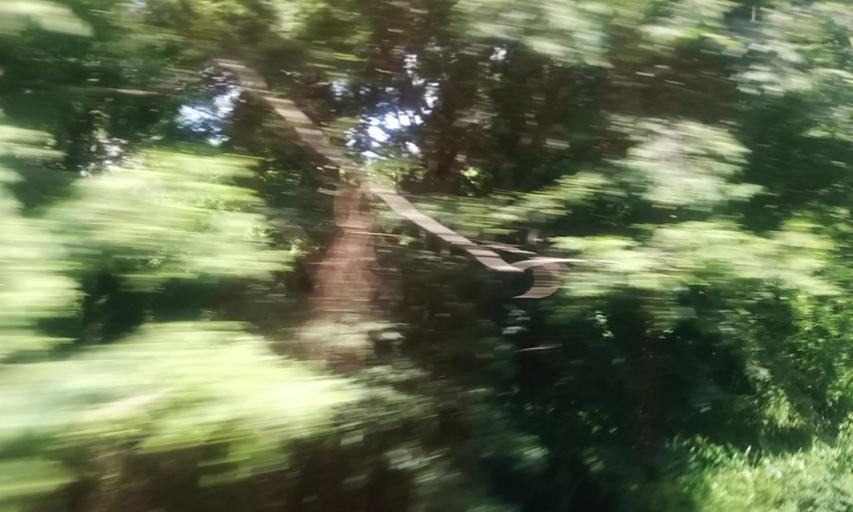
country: JP
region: Chiba
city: Chiba
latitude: 35.5667
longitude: 140.1523
